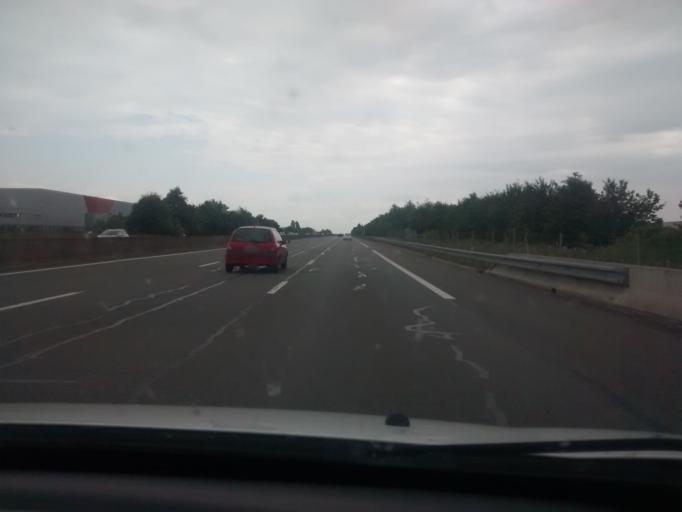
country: FR
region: Centre
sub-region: Departement d'Eure-et-Loir
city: Le Coudray
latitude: 48.4346
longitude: 1.5214
